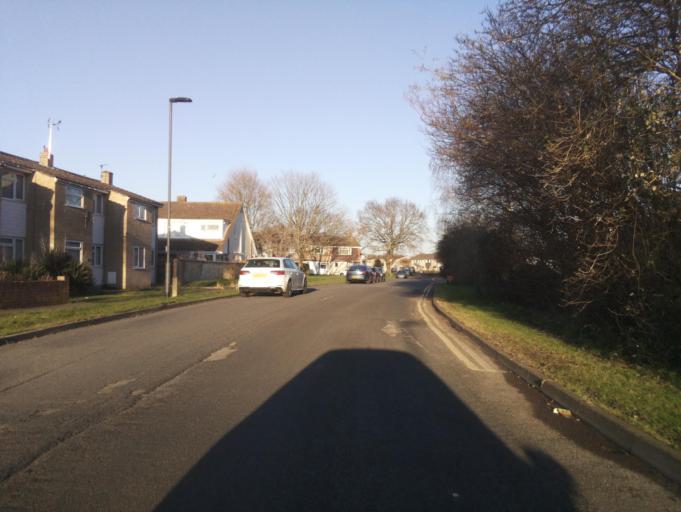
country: GB
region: England
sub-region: South Gloucestershire
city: Yate
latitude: 51.5318
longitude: -2.4278
